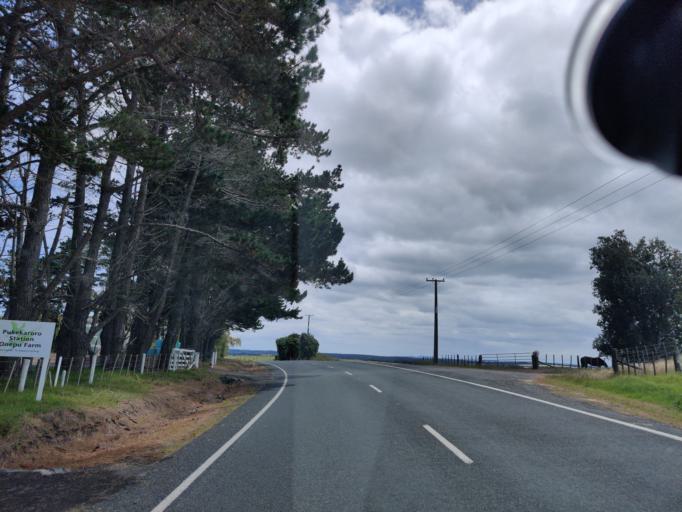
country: NZ
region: Northland
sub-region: Far North District
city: Kaitaia
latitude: -34.6944
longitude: 173.0233
